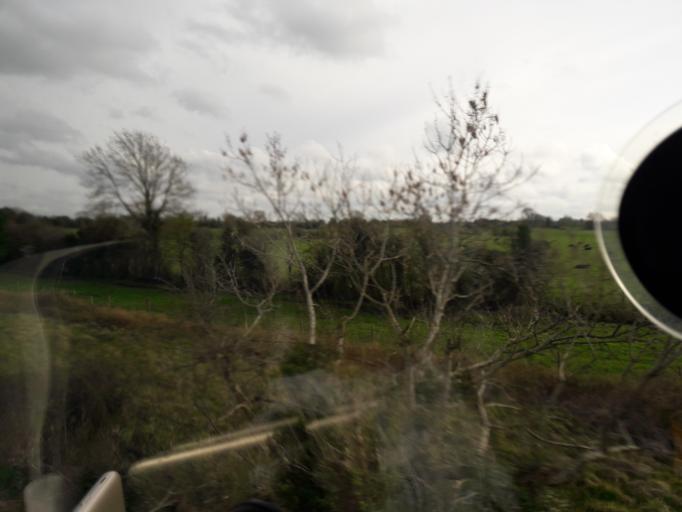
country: IE
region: Leinster
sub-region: An Mhi
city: Longwood
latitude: 53.4463
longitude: -6.9460
